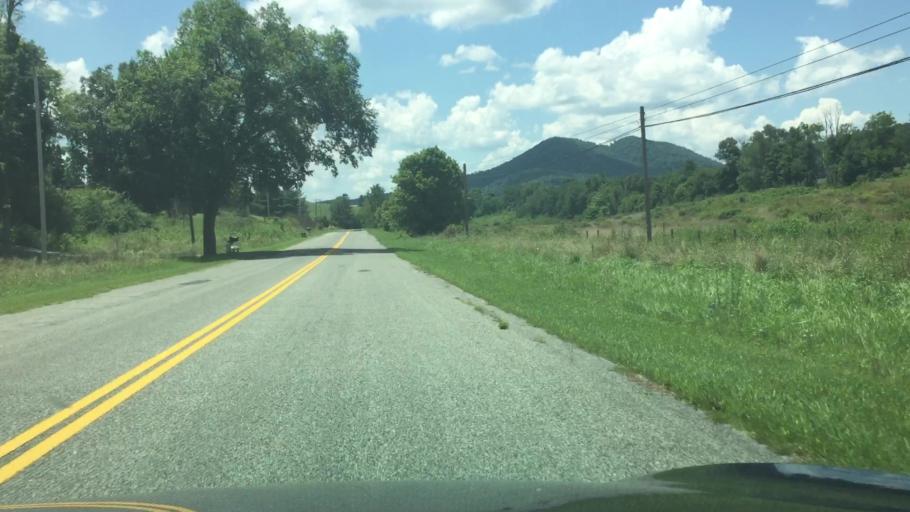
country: US
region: Virginia
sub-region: Pulaski County
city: Pulaski
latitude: 36.9807
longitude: -80.8286
